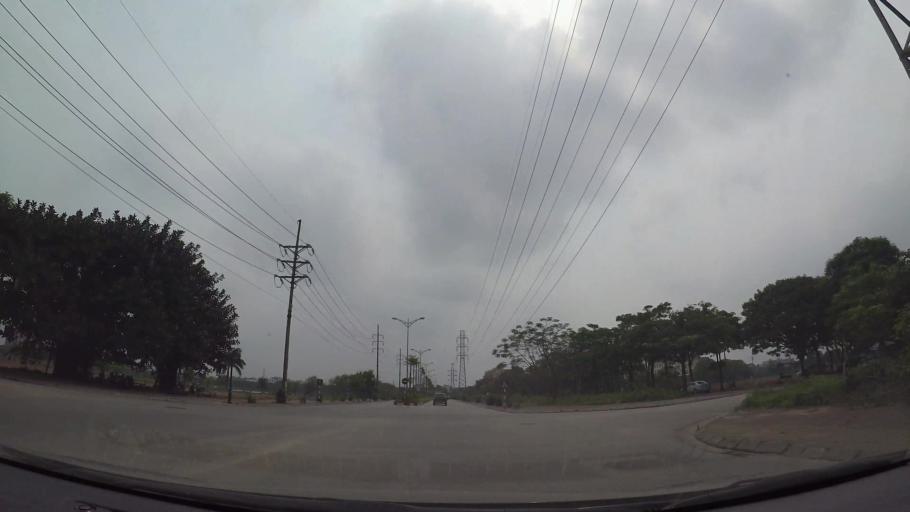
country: VN
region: Ha Noi
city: Trau Quy
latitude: 21.0644
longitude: 105.9045
